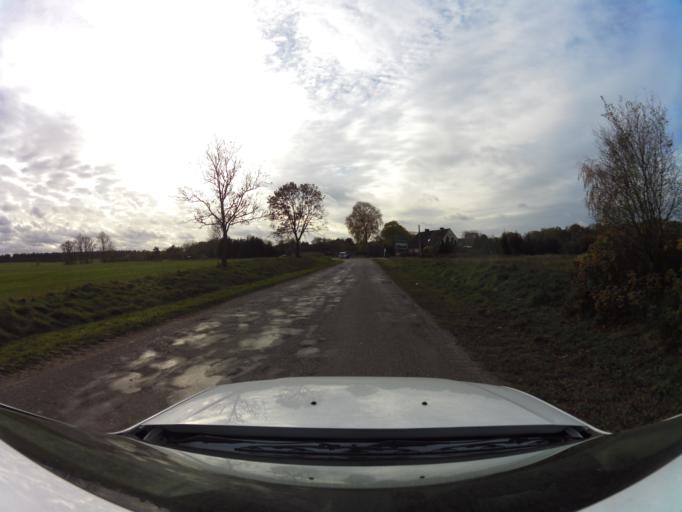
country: PL
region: West Pomeranian Voivodeship
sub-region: Powiat gryficki
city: Gryfice
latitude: 53.8707
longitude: 15.1204
